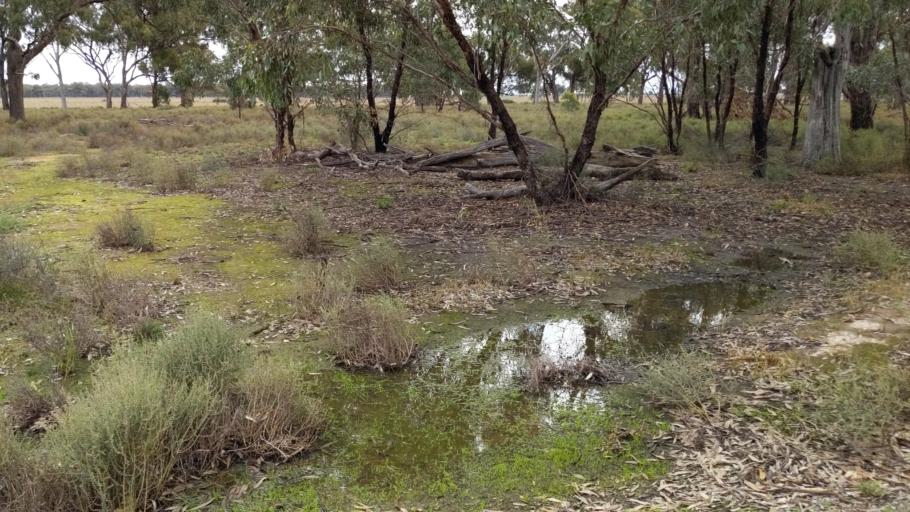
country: AU
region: New South Wales
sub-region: Coolamon
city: Coolamon
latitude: -34.8613
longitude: 146.9195
